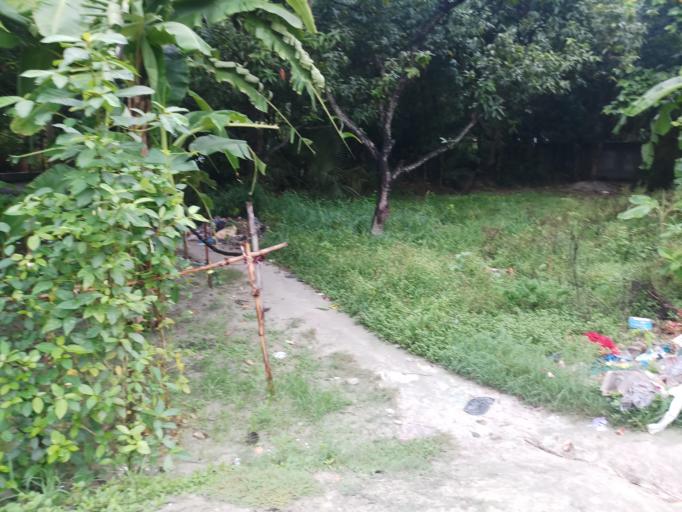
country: IN
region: Bihar
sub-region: Vaishali
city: Lalganj
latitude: 25.8469
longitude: 85.2599
